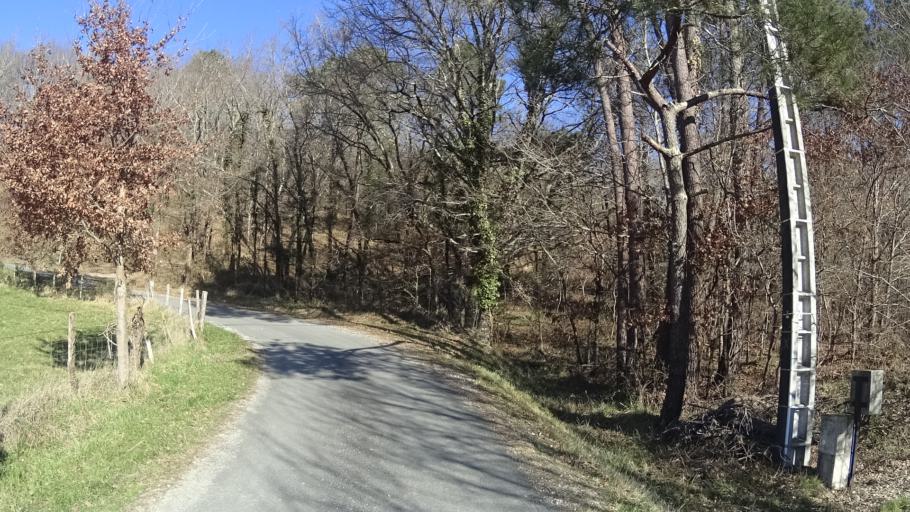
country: FR
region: Aquitaine
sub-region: Departement de la Dordogne
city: Saint-Medard-de-Mussidan
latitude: 45.0426
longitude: 0.2565
